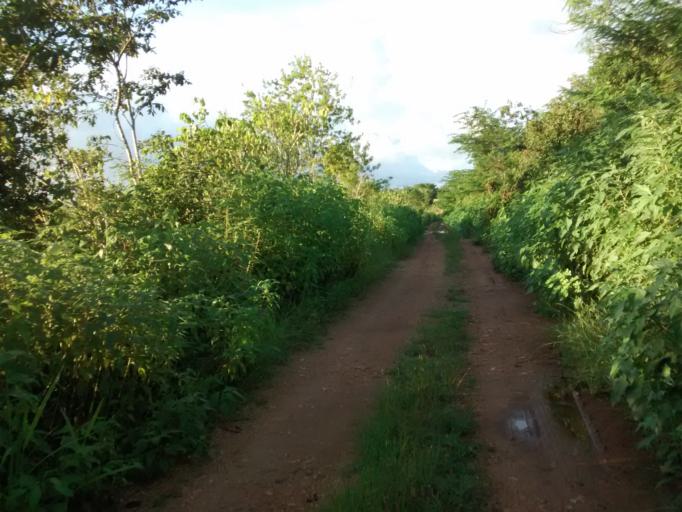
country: MX
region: Yucatan
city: Valladolid
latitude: 20.7189
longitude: -88.2062
